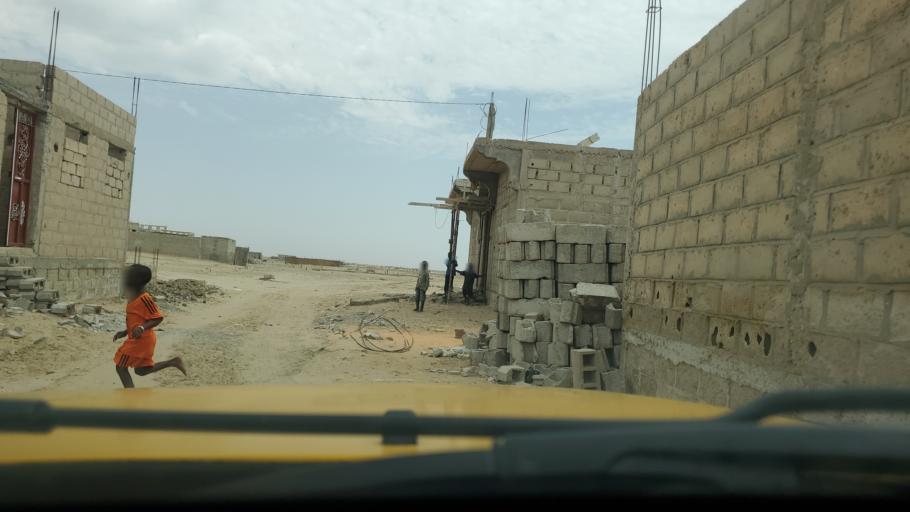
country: SN
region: Saint-Louis
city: Saint-Louis
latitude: 16.0332
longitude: -16.4620
